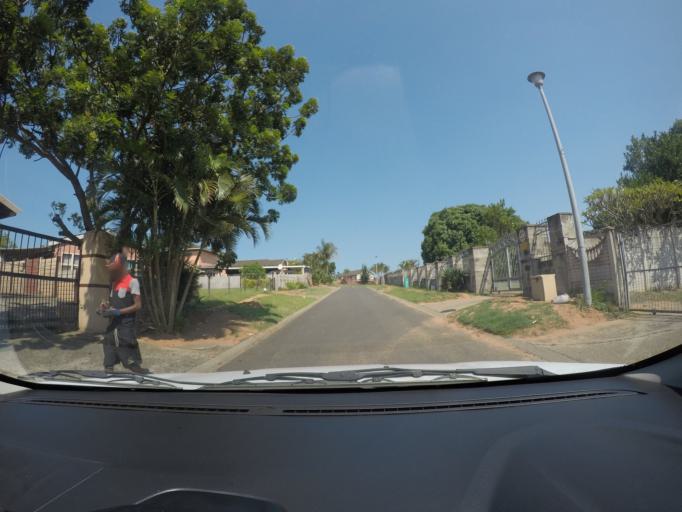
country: ZA
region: KwaZulu-Natal
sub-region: uThungulu District Municipality
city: Richards Bay
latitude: -28.7254
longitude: 32.0428
